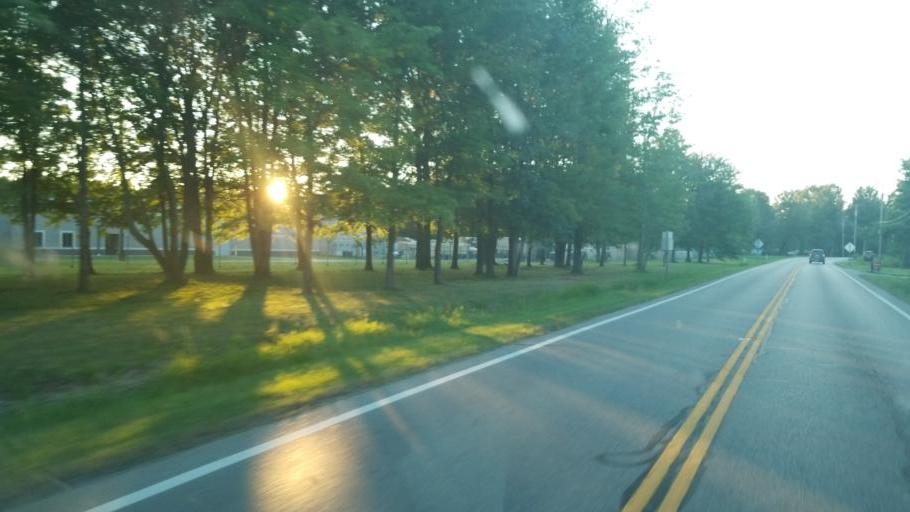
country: US
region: Ohio
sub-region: Trumbull County
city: Newton Falls
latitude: 41.2059
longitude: -80.9766
